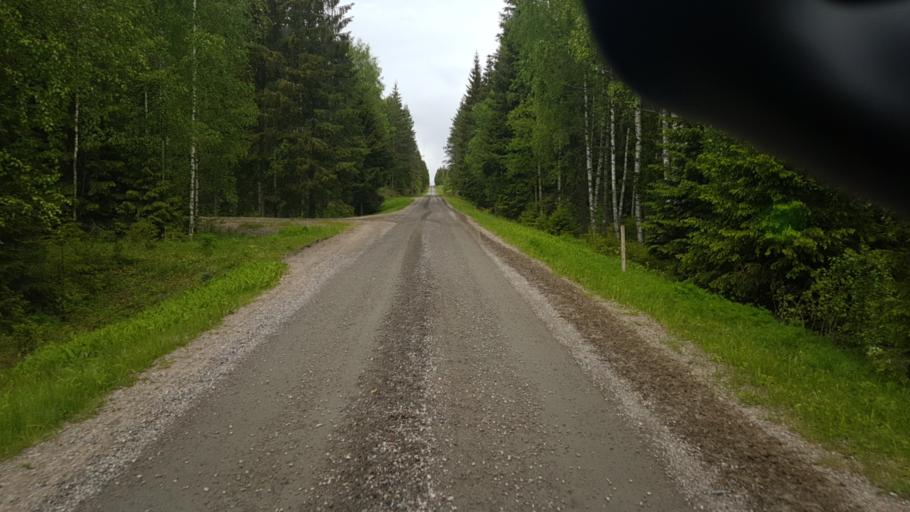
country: SE
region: Vaermland
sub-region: Eda Kommun
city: Charlottenberg
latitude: 60.0038
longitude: 12.5074
